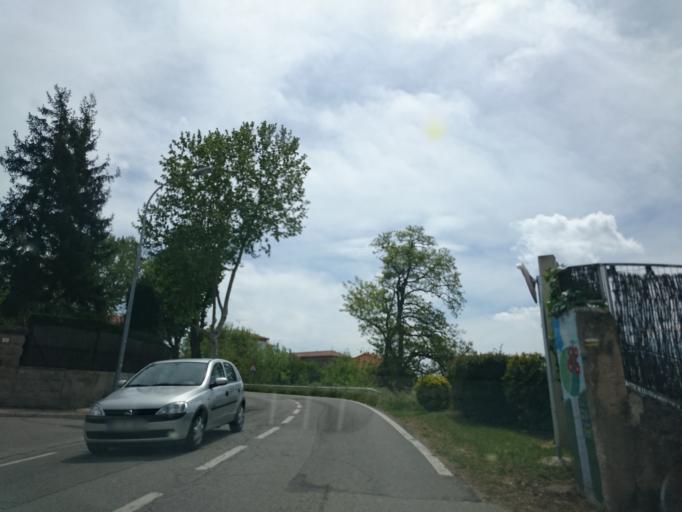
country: ES
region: Catalonia
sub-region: Provincia de Barcelona
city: Prats de Llucanes
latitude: 42.0087
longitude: 2.0319
